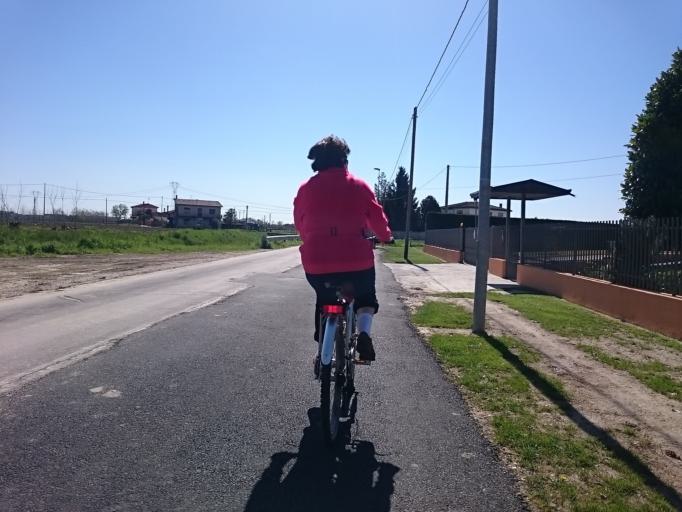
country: IT
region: Veneto
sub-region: Provincia di Padova
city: Ponte San Nicolo
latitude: 45.3585
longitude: 11.9137
